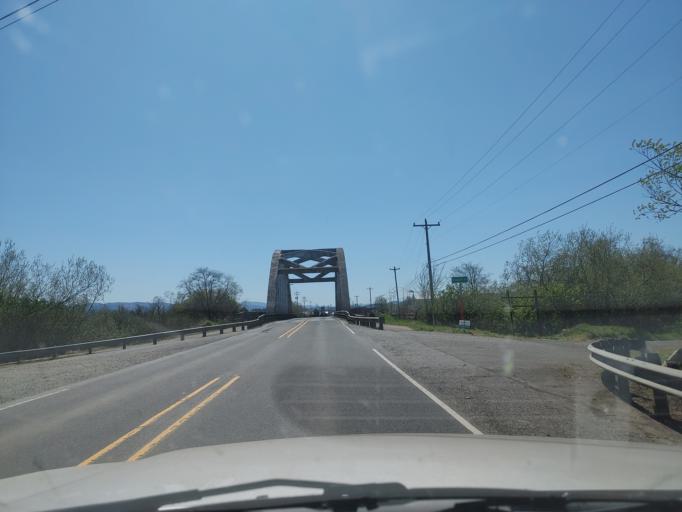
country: US
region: Oregon
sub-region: Tillamook County
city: Tillamook
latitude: 45.4790
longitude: -123.8446
